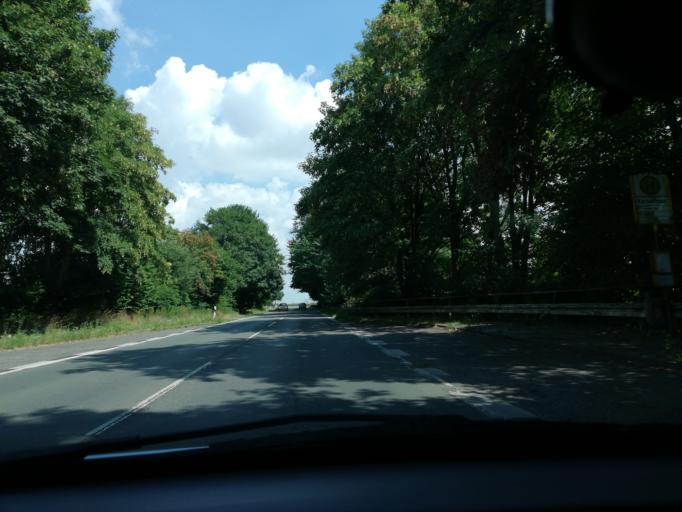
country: DE
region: North Rhine-Westphalia
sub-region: Regierungsbezirk Dusseldorf
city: Ratingen
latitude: 51.2955
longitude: 6.9073
